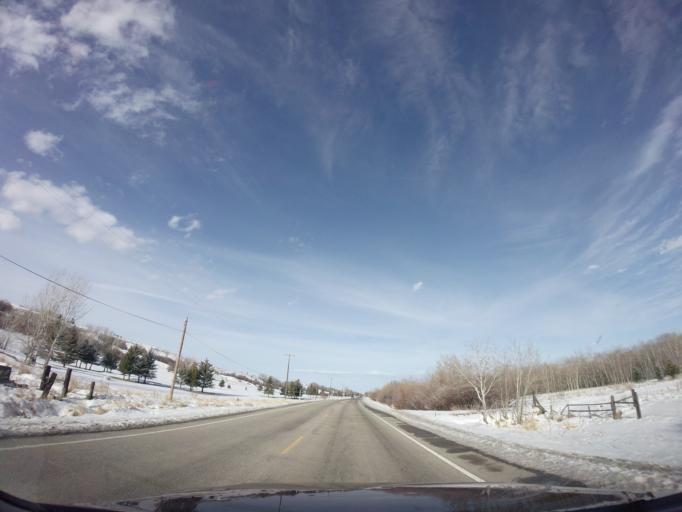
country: US
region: Montana
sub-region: Carbon County
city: Red Lodge
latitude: 45.2040
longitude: -109.2449
